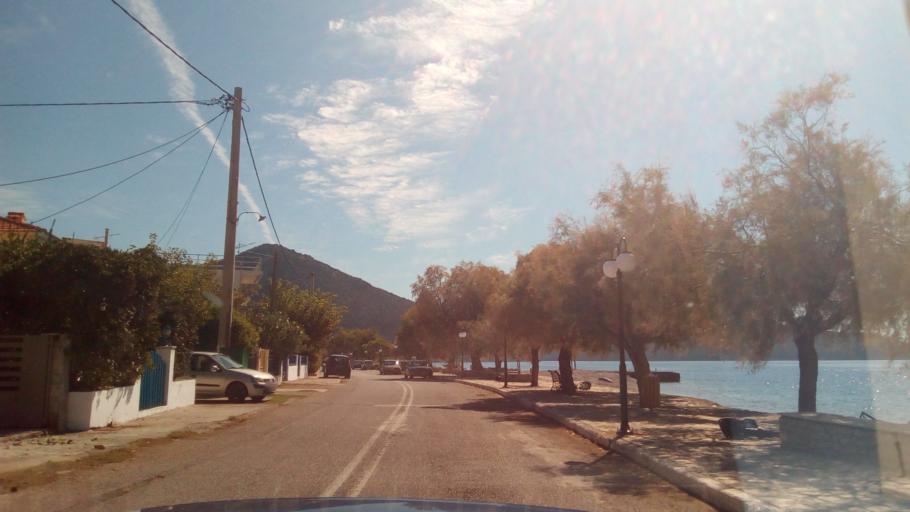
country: GR
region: West Greece
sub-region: Nomos Achaias
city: Kamarai
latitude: 38.3915
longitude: 22.0547
